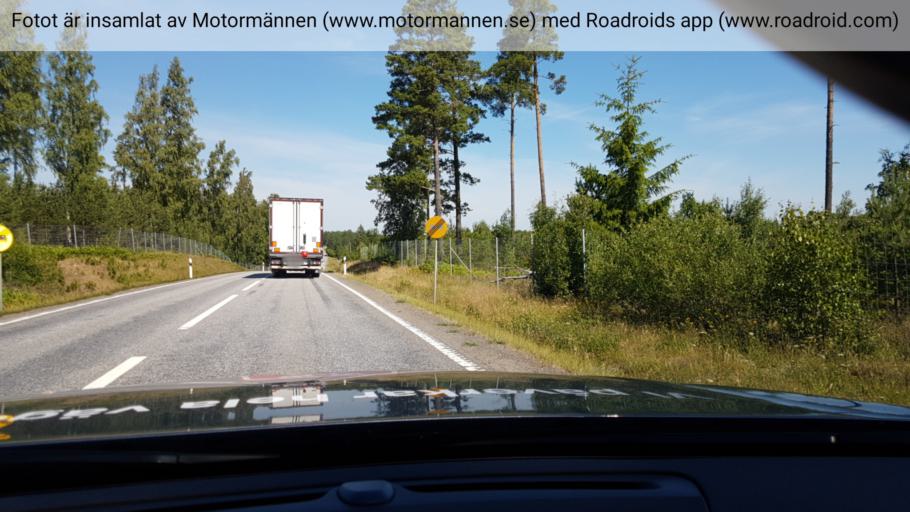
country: SE
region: OErebro
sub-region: Hallsbergs Kommun
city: Palsboda
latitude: 58.9177
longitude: 15.4343
